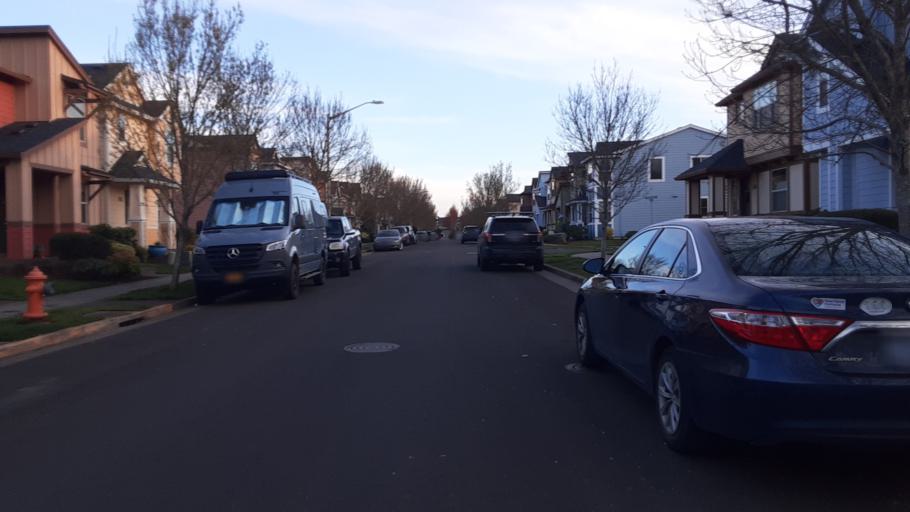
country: US
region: Oregon
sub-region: Benton County
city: Corvallis
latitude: 44.5351
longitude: -123.2544
